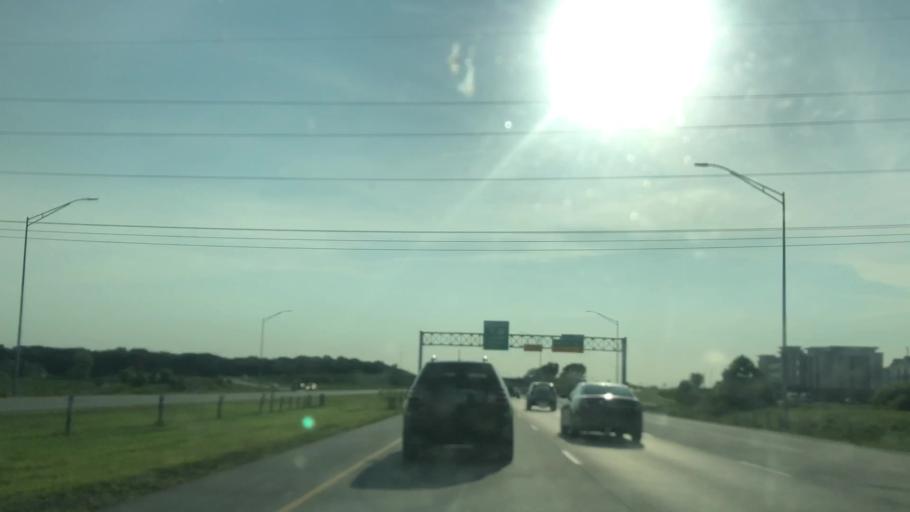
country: US
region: Iowa
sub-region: Story County
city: Ames
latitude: 42.0071
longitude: -93.5809
